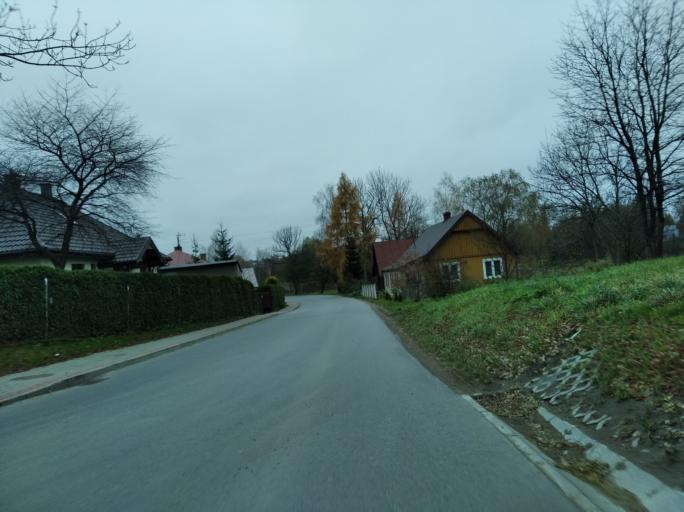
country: PL
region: Subcarpathian Voivodeship
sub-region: Powiat krosnienski
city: Chorkowka
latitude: 49.6682
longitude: 21.6867
